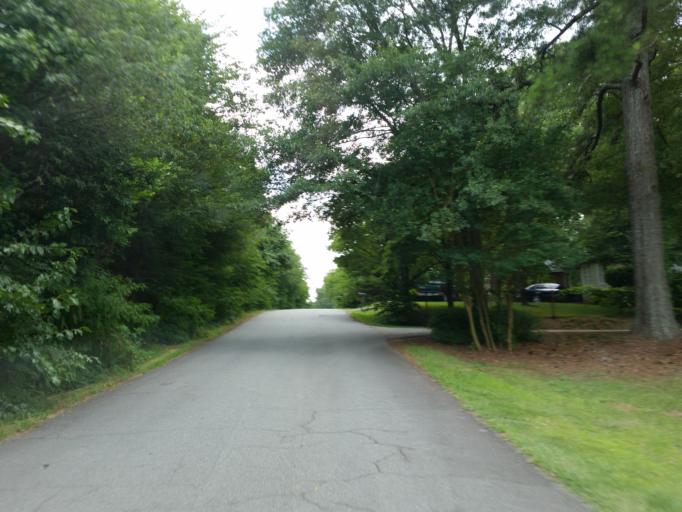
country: US
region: Georgia
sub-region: Cobb County
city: Marietta
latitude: 33.9963
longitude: -84.5178
